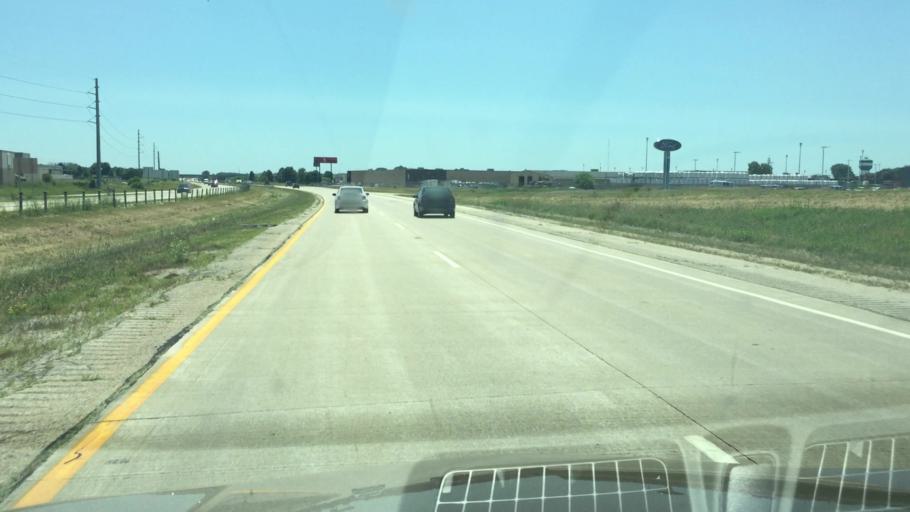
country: US
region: Wisconsin
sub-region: Dodge County
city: Beaver Dam
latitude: 43.4853
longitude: -88.8152
